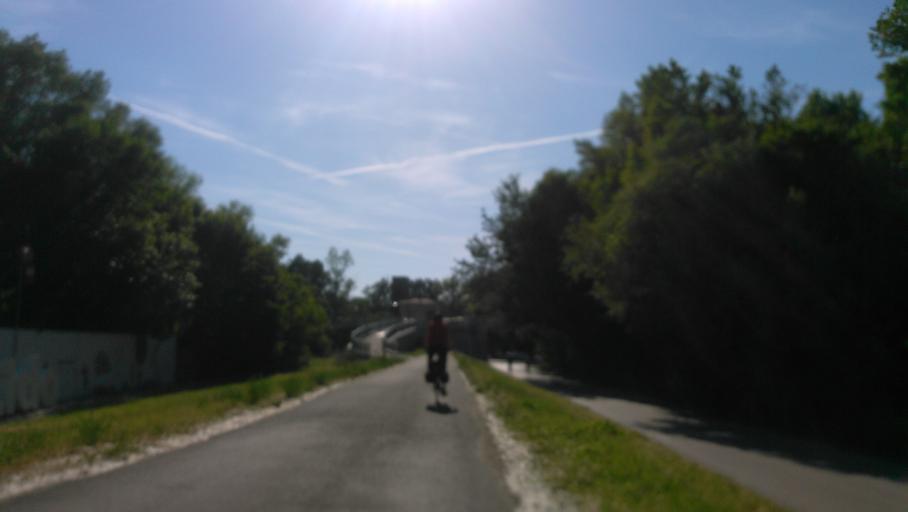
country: SK
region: Bratislavsky
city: Bratislava
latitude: 48.1358
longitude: 17.1194
